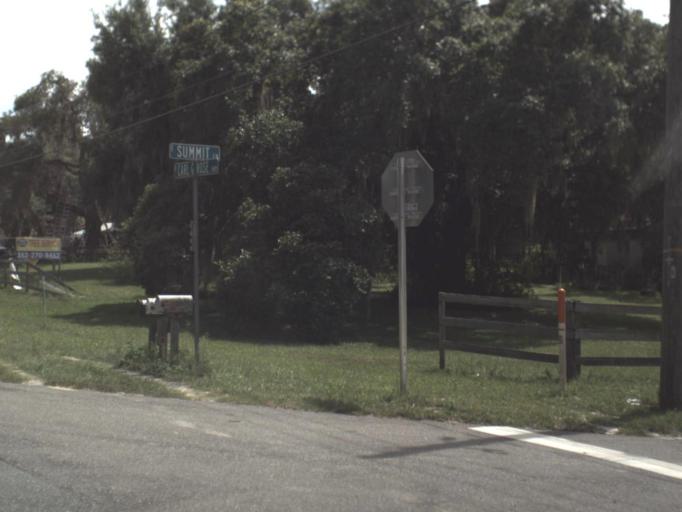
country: US
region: Florida
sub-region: Citrus County
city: Hernando
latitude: 28.9133
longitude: -82.3754
